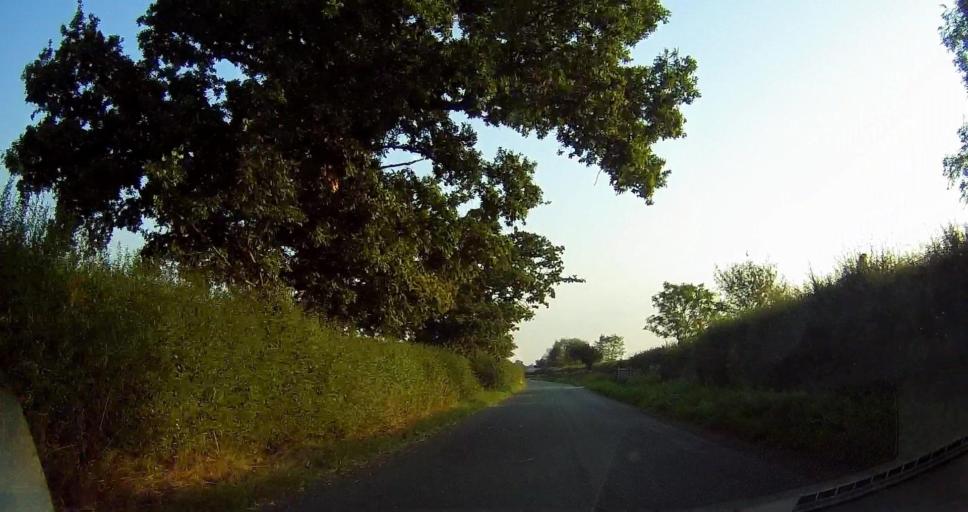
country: GB
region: England
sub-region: Cheshire East
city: Nantwich
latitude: 53.0329
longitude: -2.5175
